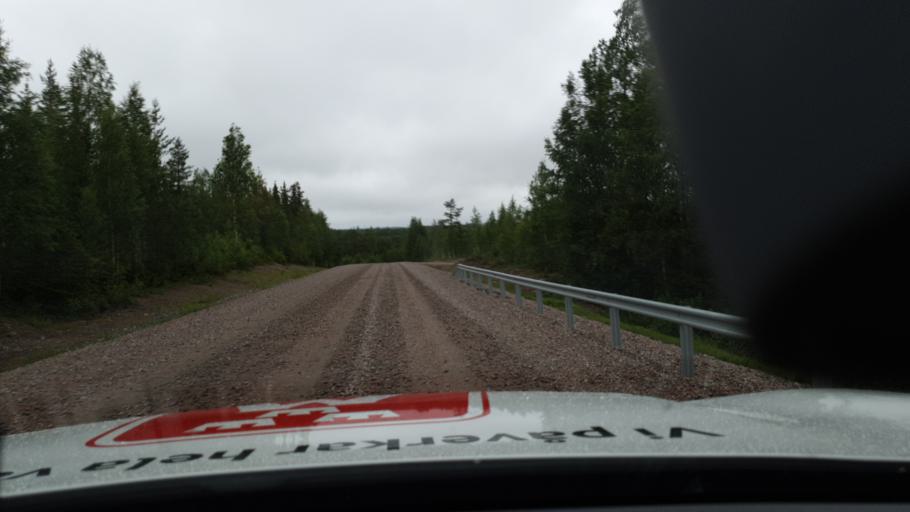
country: SE
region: Norrbotten
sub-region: Overtornea Kommun
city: OEvertornea
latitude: 66.4558
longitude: 23.4824
